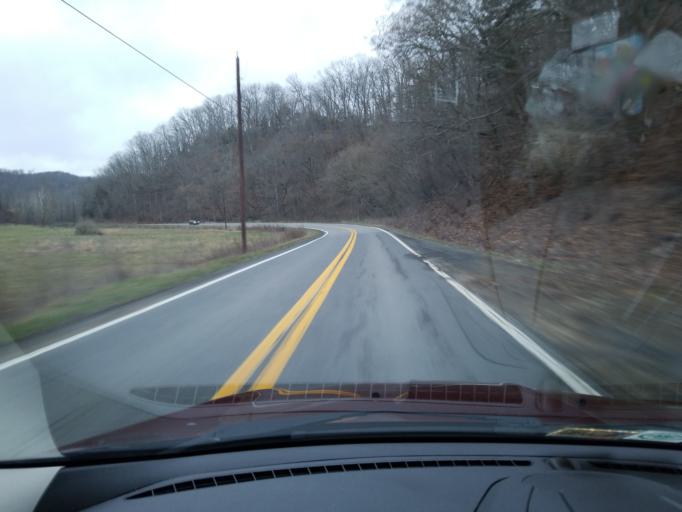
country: US
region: West Virginia
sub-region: Monroe County
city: Union
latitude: 37.5470
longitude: -80.5788
